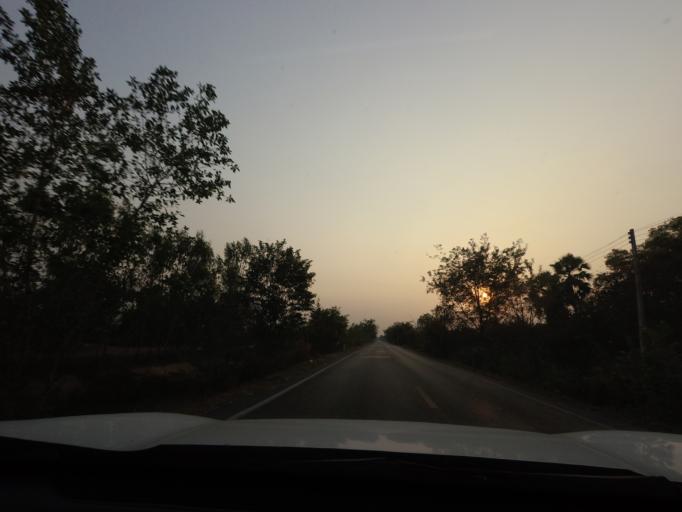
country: TH
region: Nakhon Nayok
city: Ongkharak
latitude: 14.1529
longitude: 101.0402
